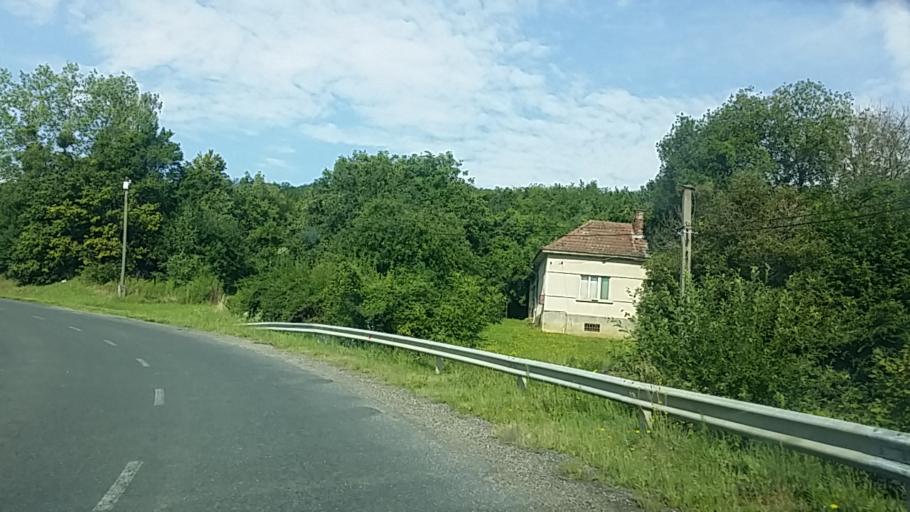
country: HU
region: Zala
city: Letenye
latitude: 46.5280
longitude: 16.7247
